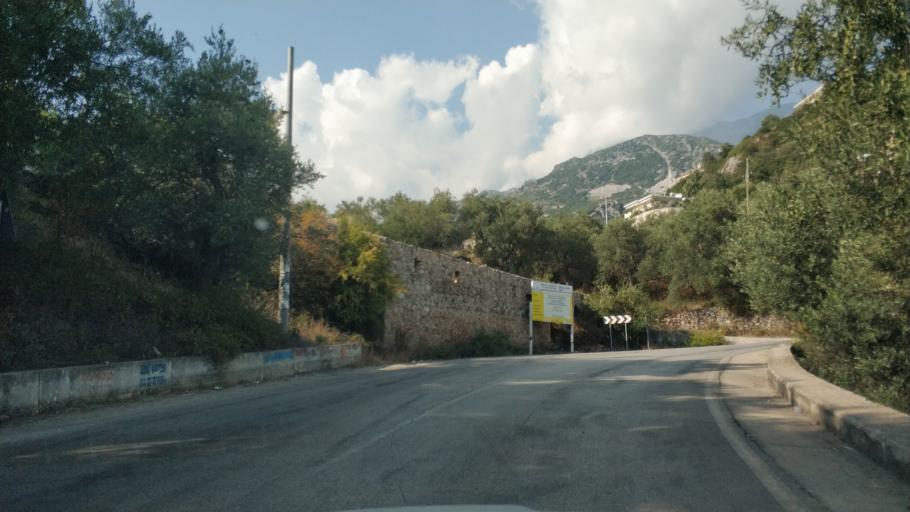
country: AL
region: Vlore
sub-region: Rrethi i Vlores
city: Vranisht
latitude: 40.1525
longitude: 19.6332
